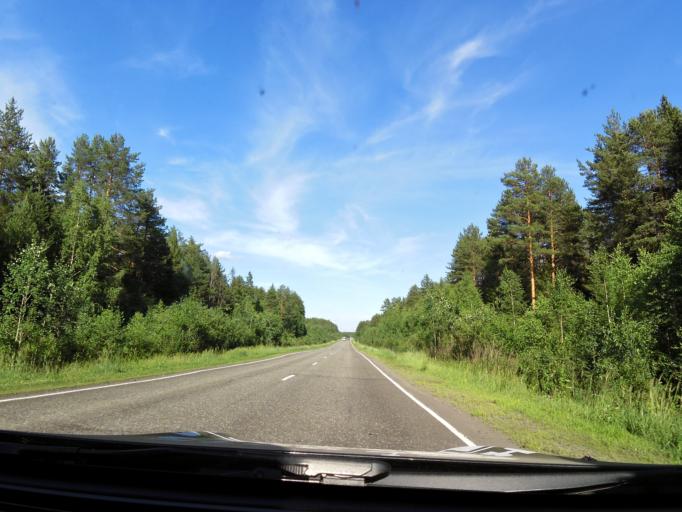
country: RU
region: Kirov
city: Dubrovka
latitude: 58.9063
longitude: 51.2263
